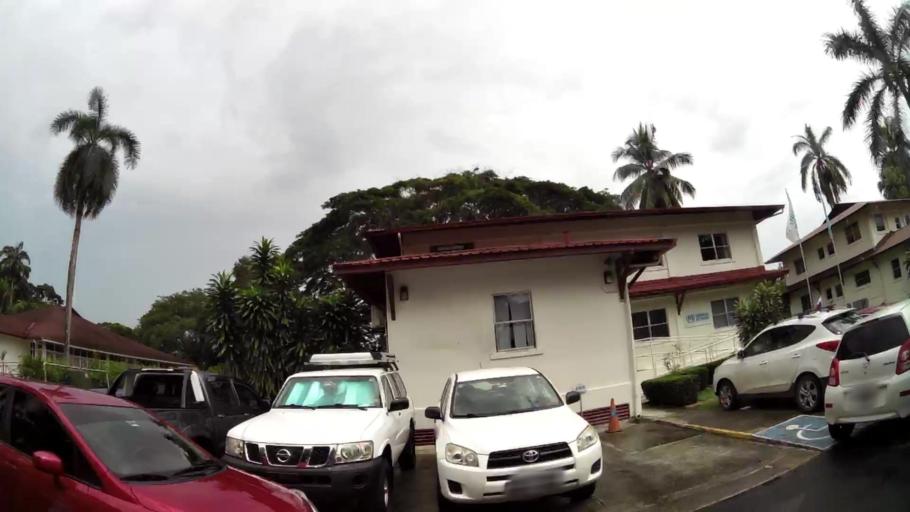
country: PA
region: Panama
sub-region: Distrito de Panama
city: Ancon
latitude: 8.9976
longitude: -79.5797
